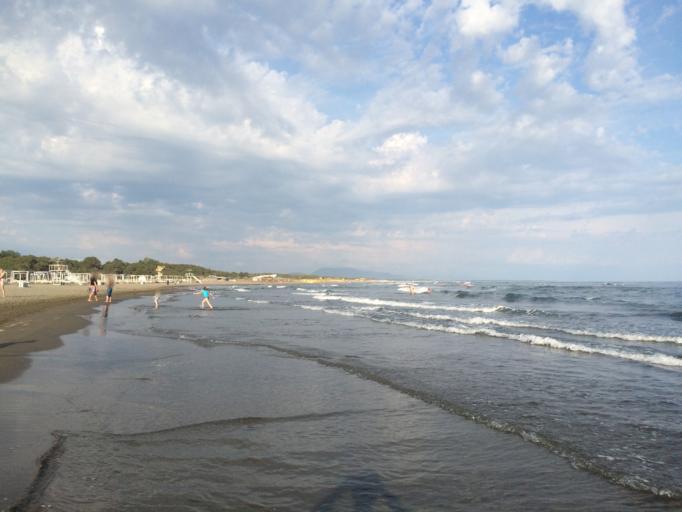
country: ME
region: Ulcinj
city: Ulcinj
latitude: 41.9093
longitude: 19.2376
